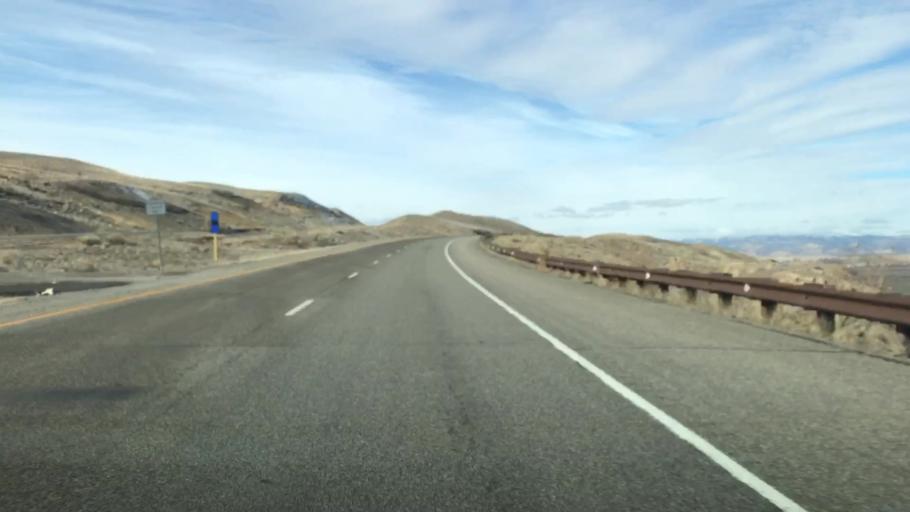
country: US
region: Colorado
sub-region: Mesa County
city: Loma
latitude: 39.2244
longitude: -108.8939
